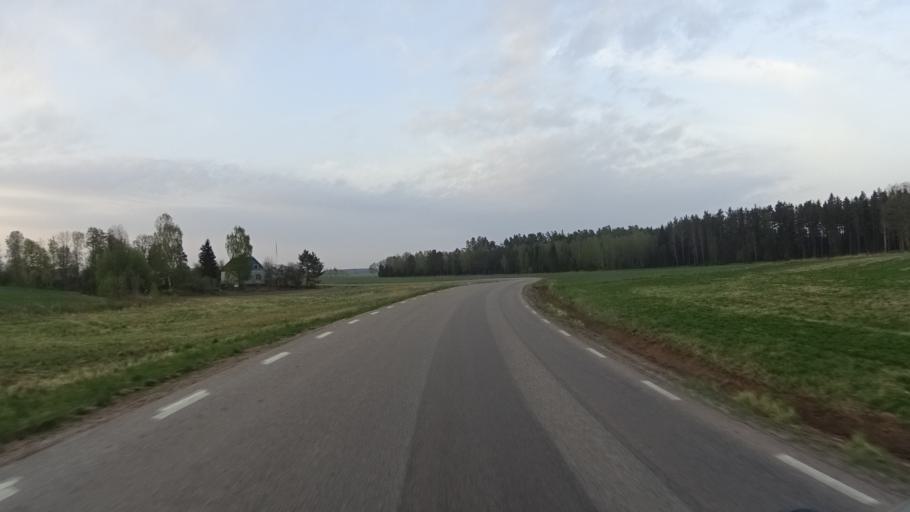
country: SE
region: Vaestra Goetaland
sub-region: Gotene Kommun
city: Kallby
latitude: 58.4825
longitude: 13.3166
